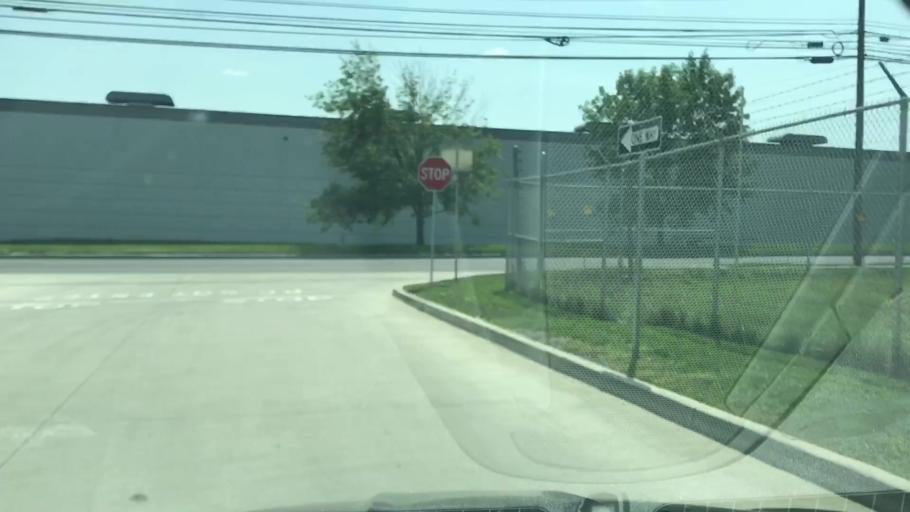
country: US
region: Pennsylvania
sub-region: Northampton County
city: Middletown
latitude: 40.6794
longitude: -75.3608
